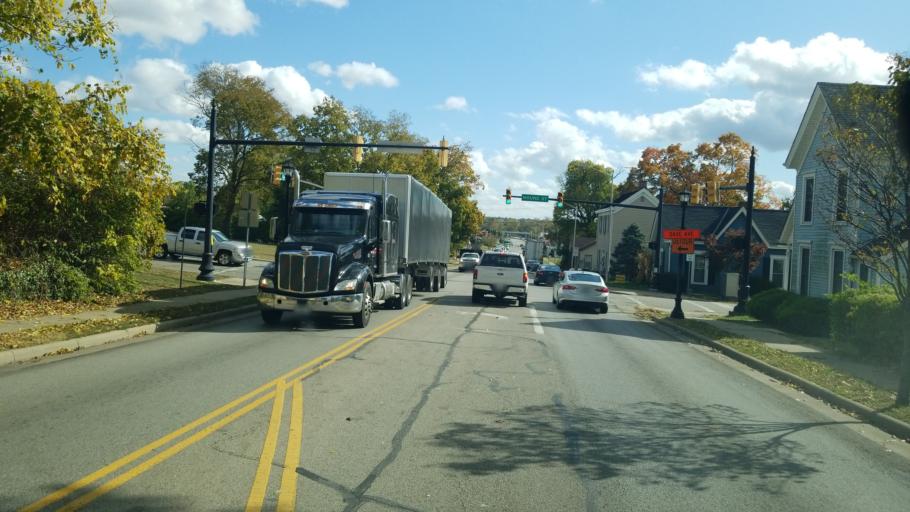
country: US
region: Ohio
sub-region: Warren County
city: Lebanon
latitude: 39.4327
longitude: -84.1997
